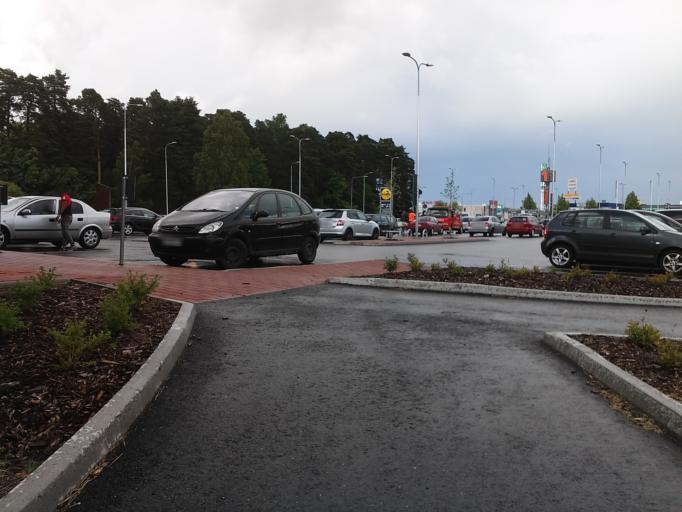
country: FI
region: Varsinais-Suomi
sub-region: Turku
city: Raisio
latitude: 60.4721
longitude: 22.2193
